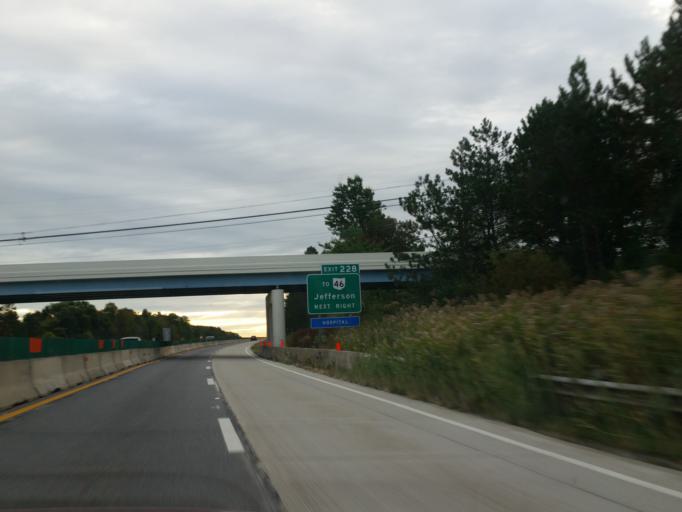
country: US
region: Ohio
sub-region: Ashtabula County
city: Ashtabula
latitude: 41.8277
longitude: -80.7858
